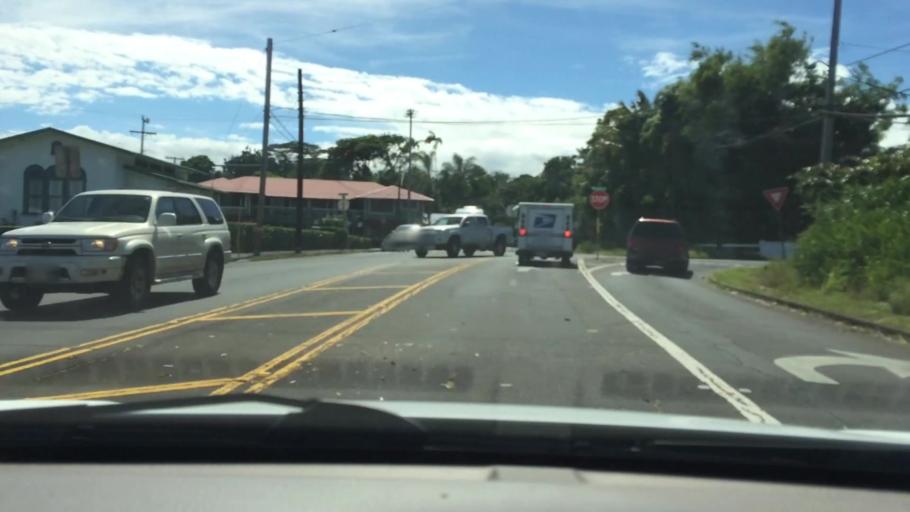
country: US
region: Hawaii
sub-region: Hawaii County
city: Hilo
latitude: 19.7260
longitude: -155.0900
